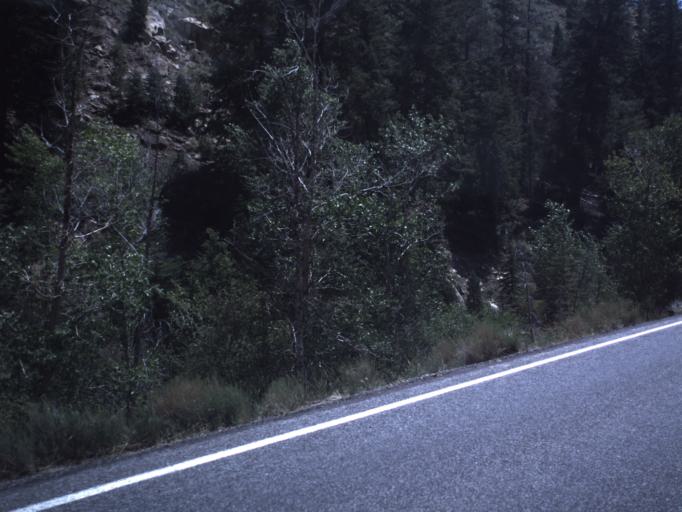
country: US
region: Utah
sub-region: Emery County
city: Huntington
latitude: 39.4599
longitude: -111.1442
